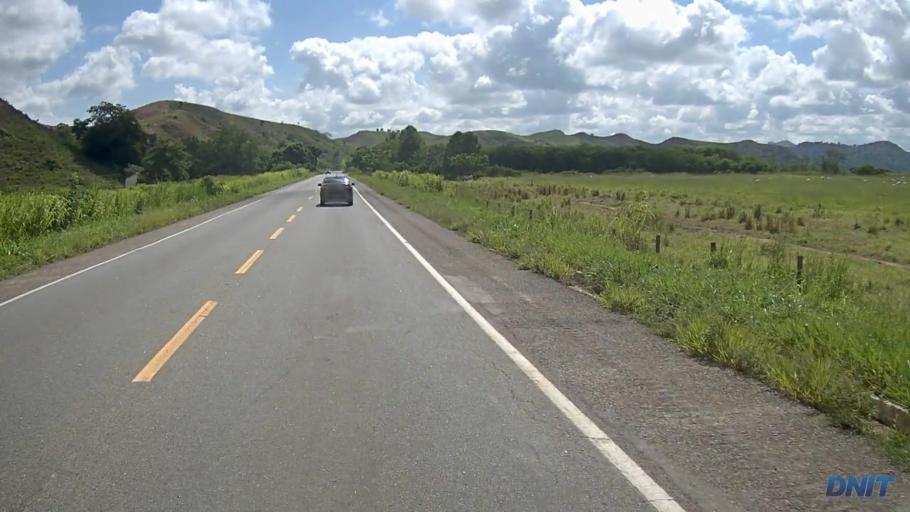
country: BR
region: Minas Gerais
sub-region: Belo Oriente
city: Belo Oriente
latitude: -19.1421
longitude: -42.2247
